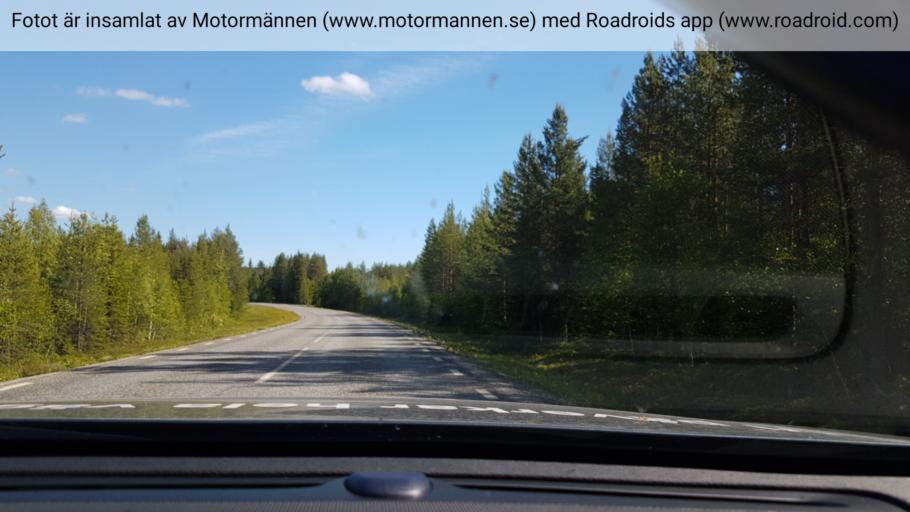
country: SE
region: Vaesterbotten
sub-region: Lycksele Kommun
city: Lycksele
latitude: 64.5878
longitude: 18.5629
